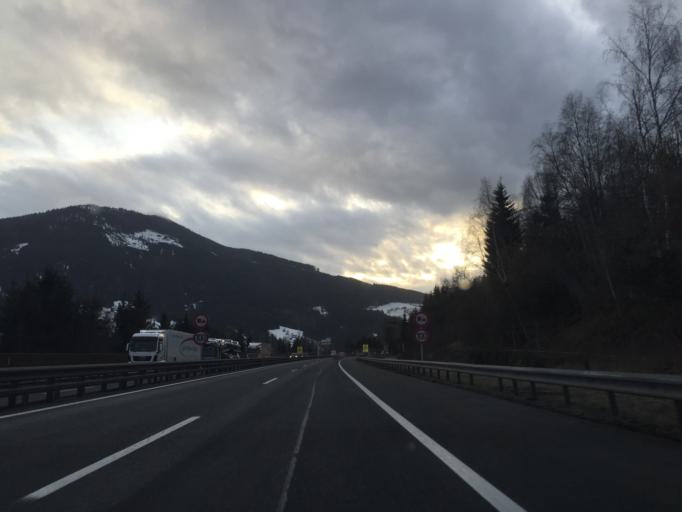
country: AT
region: Salzburg
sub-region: Politischer Bezirk Sankt Johann im Pongau
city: Huttau
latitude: 47.4207
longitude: 13.3219
